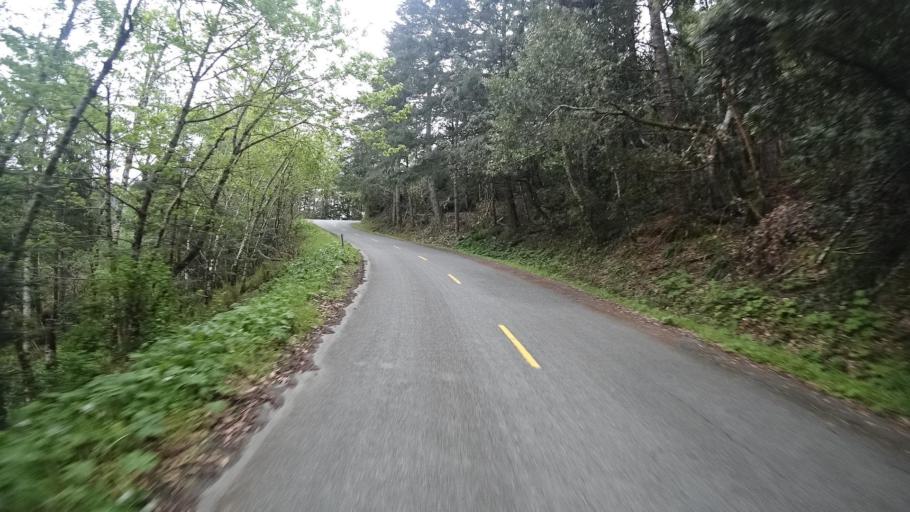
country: US
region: California
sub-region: Humboldt County
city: Blue Lake
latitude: 40.9325
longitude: -123.8460
